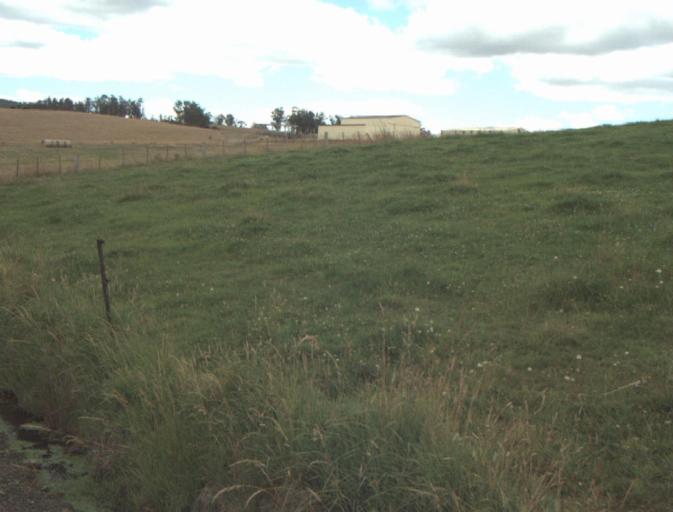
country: AU
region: Tasmania
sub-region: Launceston
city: Mayfield
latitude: -41.2399
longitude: 147.2062
